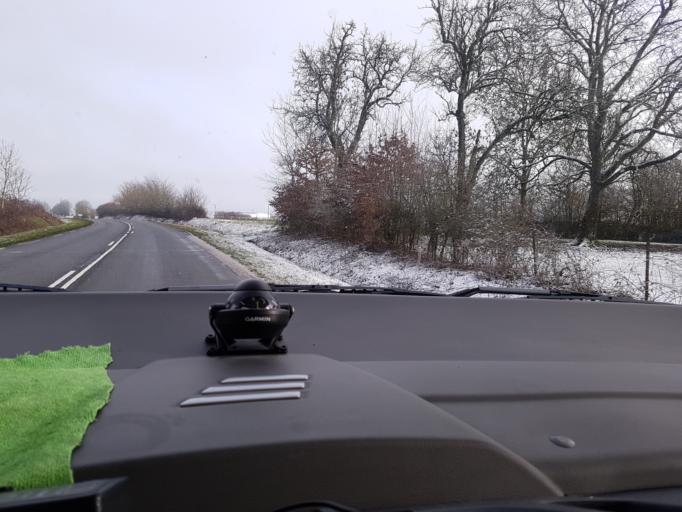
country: FR
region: Champagne-Ardenne
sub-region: Departement des Ardennes
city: Signy-le-Petit
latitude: 49.8712
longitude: 4.3385
